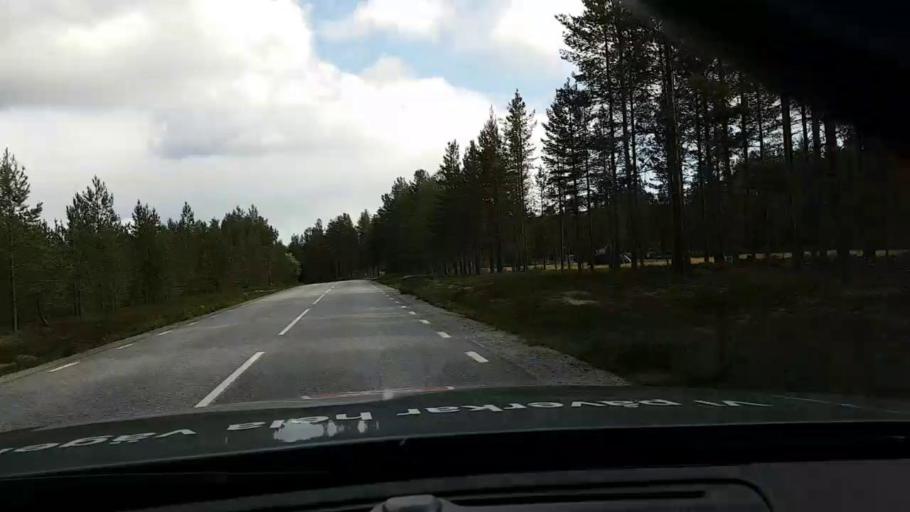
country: SE
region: Vaesternorrland
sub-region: OErnskoeldsviks Kommun
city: Bredbyn
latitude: 63.6745
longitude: 17.7980
